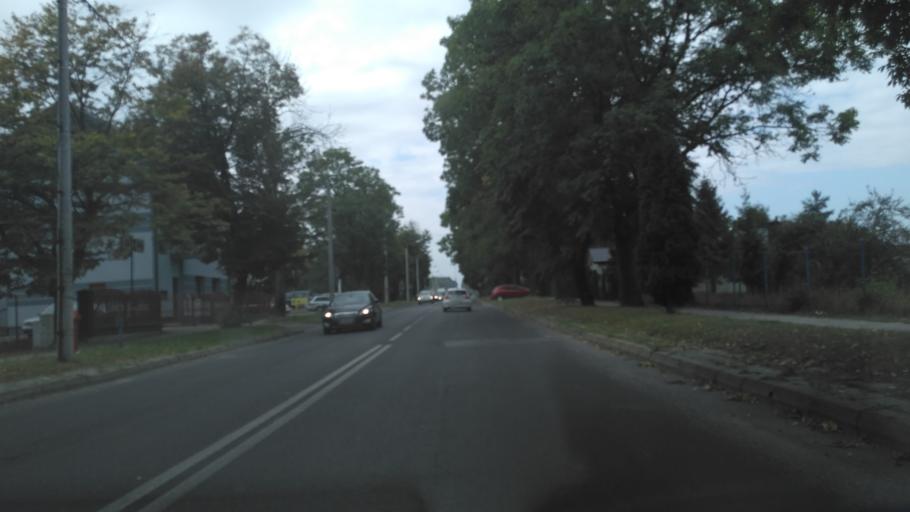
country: PL
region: Lublin Voivodeship
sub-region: Chelm
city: Chelm
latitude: 51.1444
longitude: 23.4423
